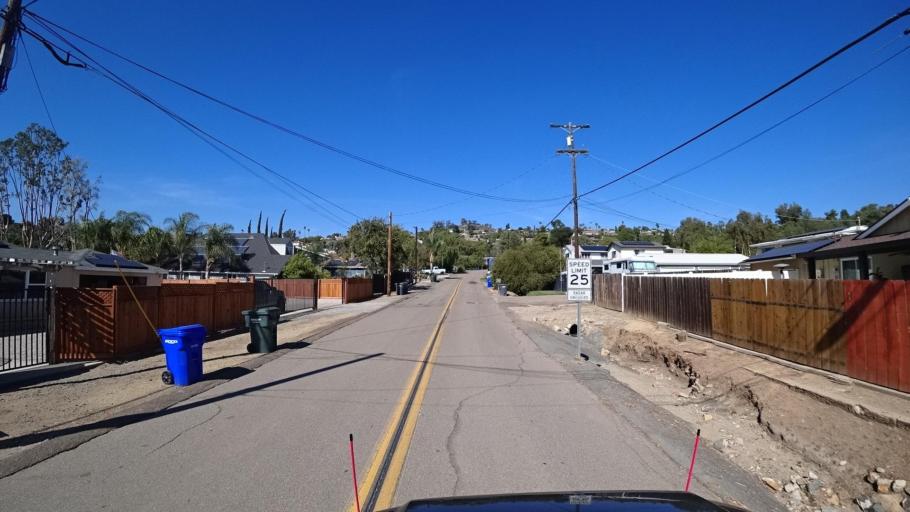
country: US
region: California
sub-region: San Diego County
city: Spring Valley
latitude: 32.7517
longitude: -116.9833
